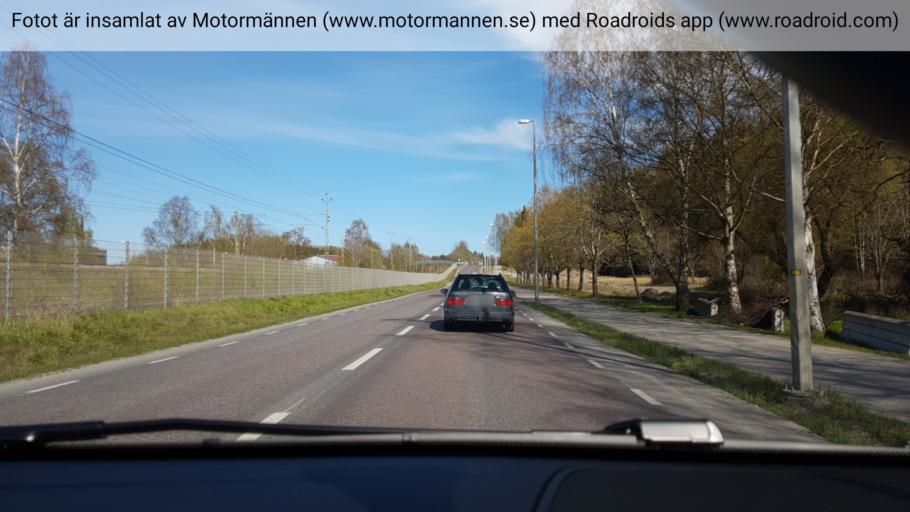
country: SE
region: Stockholm
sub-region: Botkyrka Kommun
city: Tumba
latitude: 59.1992
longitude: 17.8481
